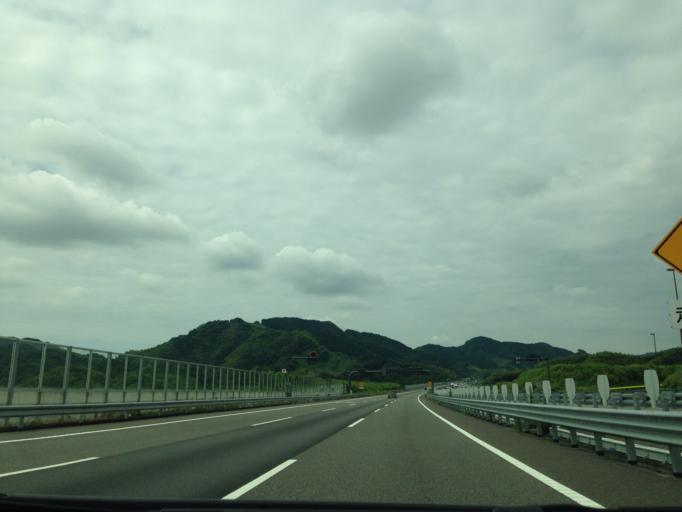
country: JP
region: Shizuoka
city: Fujieda
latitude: 34.9015
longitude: 138.2452
